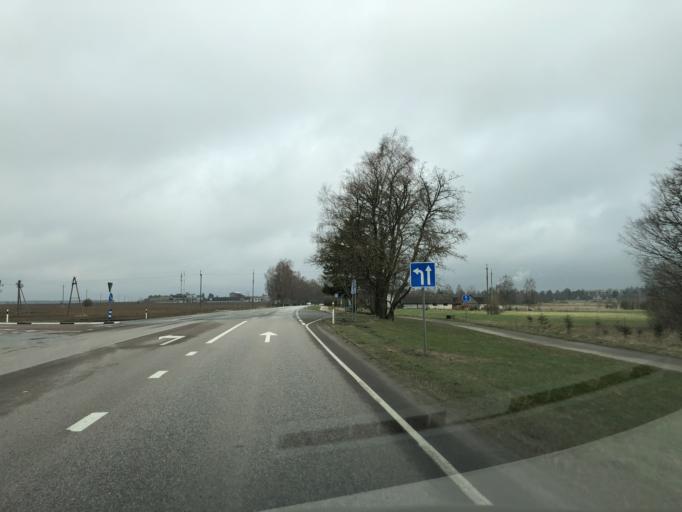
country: EE
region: Jogevamaa
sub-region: Jogeva linn
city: Jogeva
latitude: 58.7295
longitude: 26.3836
